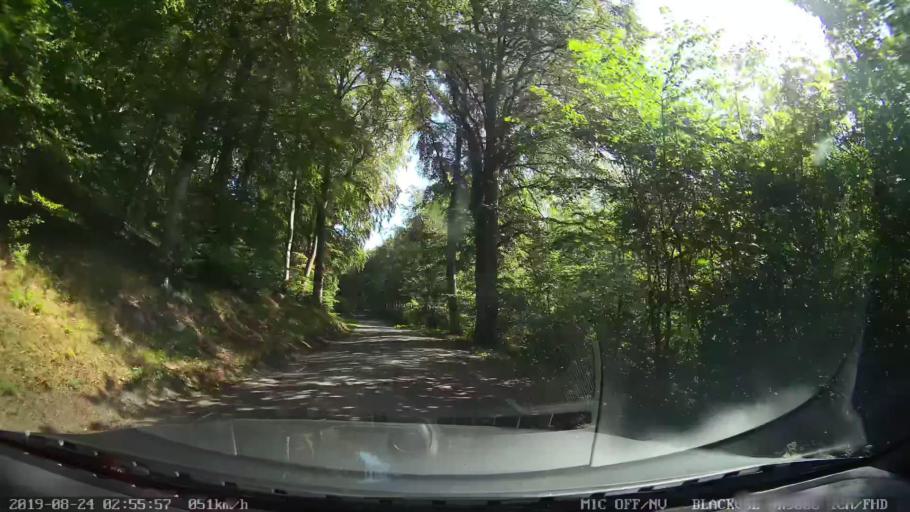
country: SE
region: Skane
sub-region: Trelleborgs Kommun
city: Anderslov
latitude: 55.4924
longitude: 13.3904
